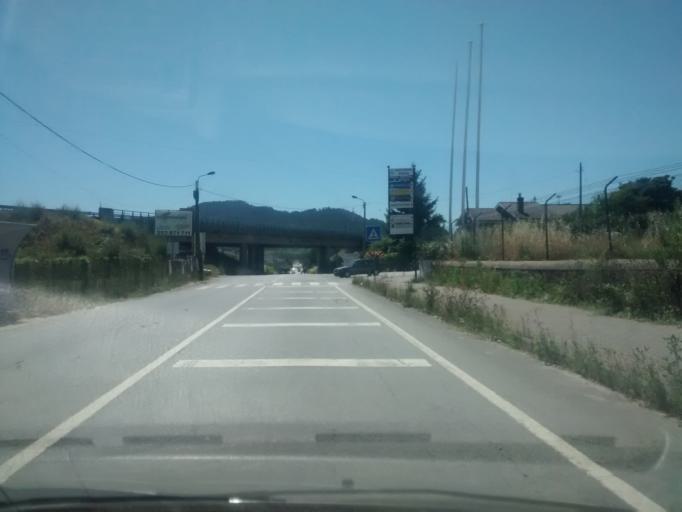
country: PT
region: Braga
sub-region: Braga
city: Oliveira
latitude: 41.5314
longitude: -8.4764
